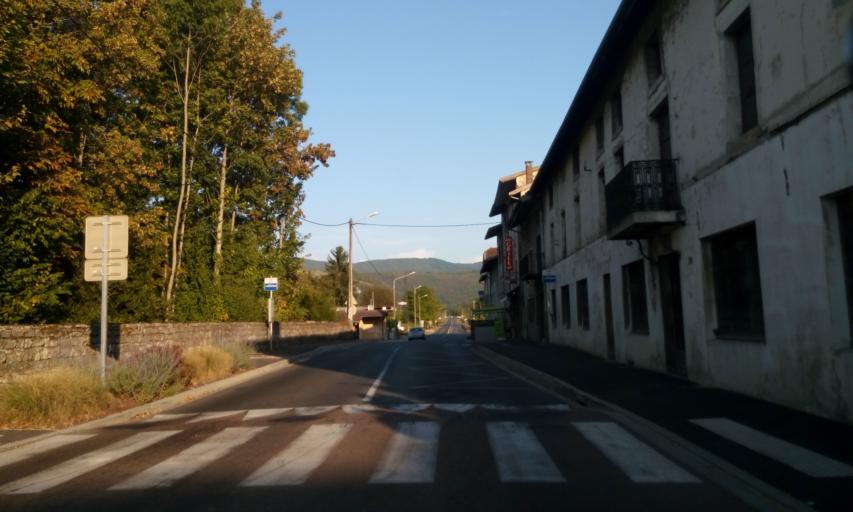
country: FR
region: Rhone-Alpes
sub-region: Departement de l'Ain
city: Poncin
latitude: 46.0827
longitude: 5.4068
